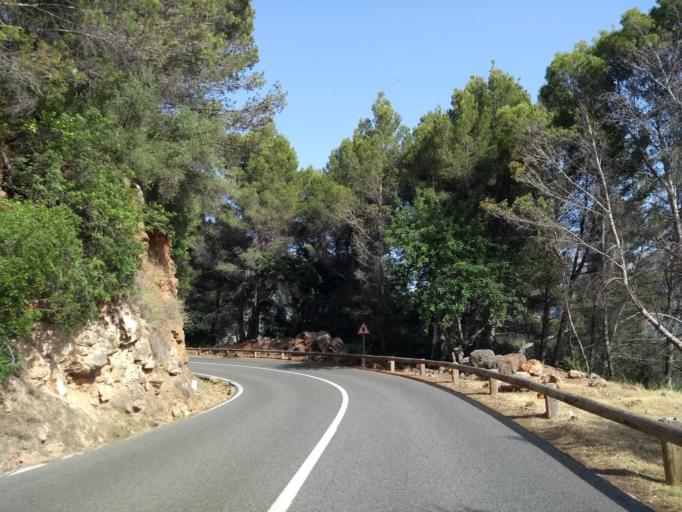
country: ES
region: Balearic Islands
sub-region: Illes Balears
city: Fornalutx
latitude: 39.7837
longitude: 2.7310
